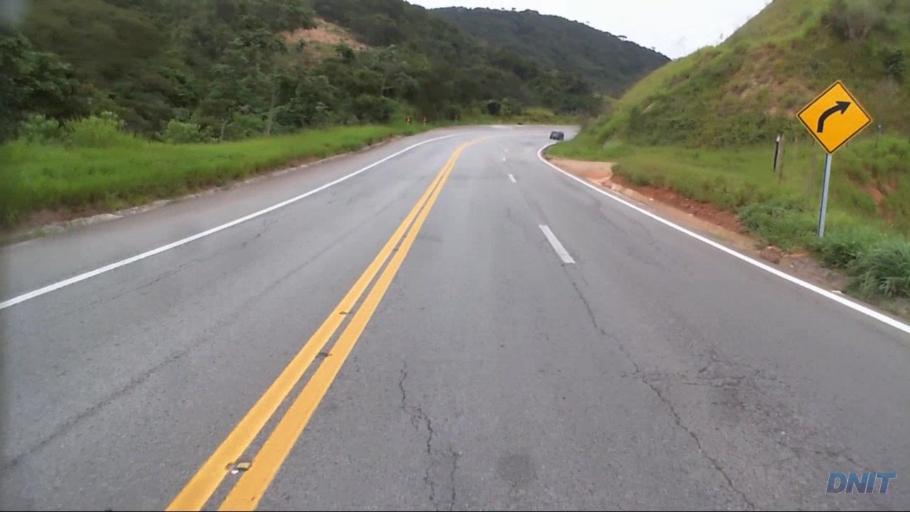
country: BR
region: Minas Gerais
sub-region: Timoteo
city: Timoteo
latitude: -19.6227
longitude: -42.8552
